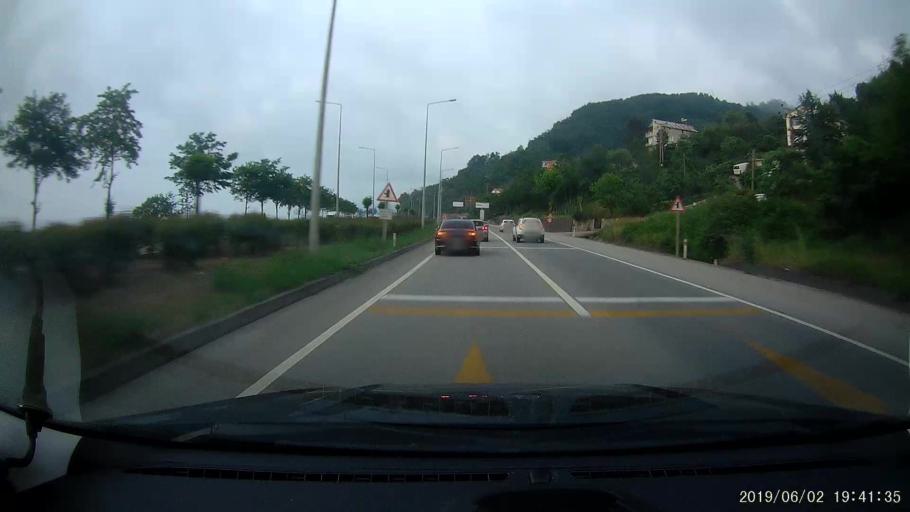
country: TR
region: Giresun
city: Kesap
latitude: 40.9134
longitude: 38.4834
